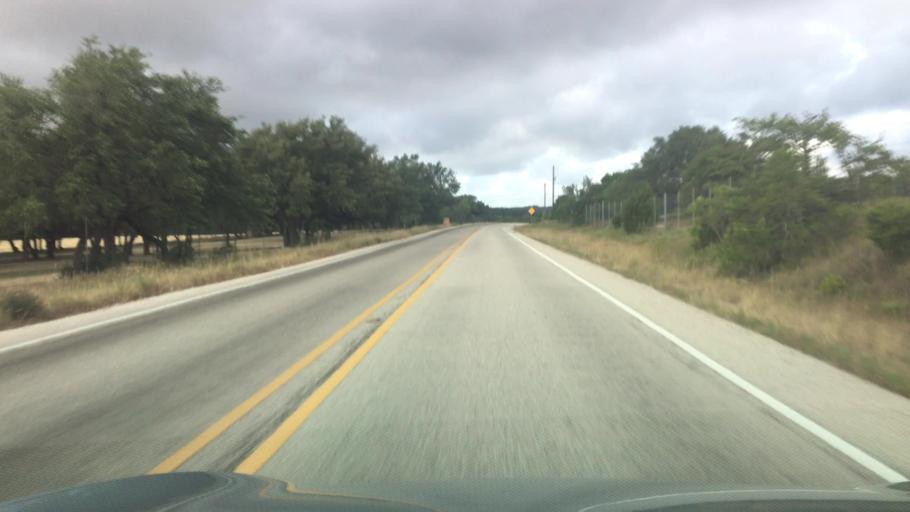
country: US
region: Texas
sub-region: Hays County
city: Dripping Springs
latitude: 30.1509
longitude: -98.2549
